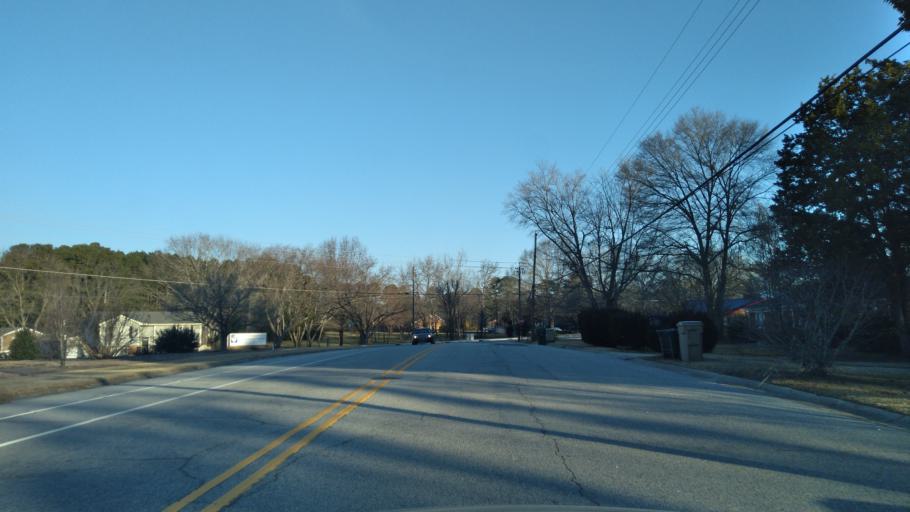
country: US
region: North Carolina
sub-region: Wake County
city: Garner
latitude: 35.7042
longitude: -78.6262
